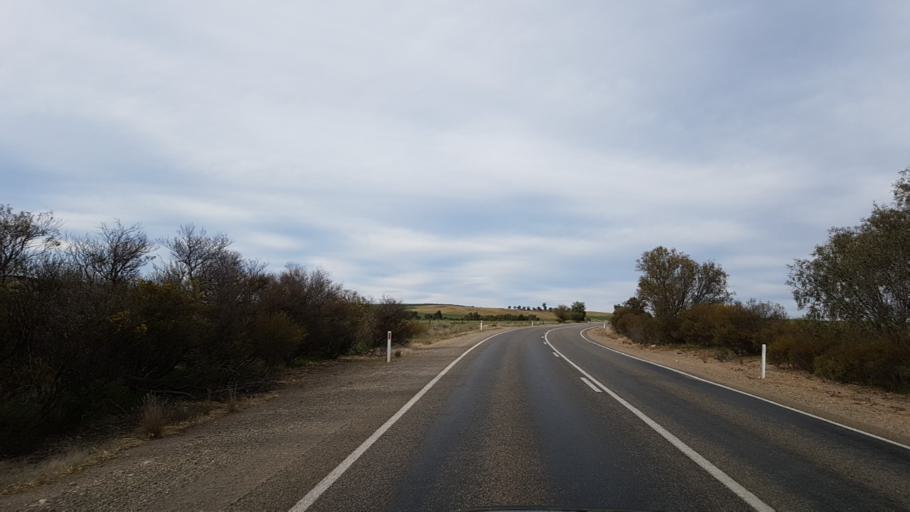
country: AU
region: South Australia
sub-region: Northern Areas
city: Jamestown
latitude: -33.2115
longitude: 138.4236
